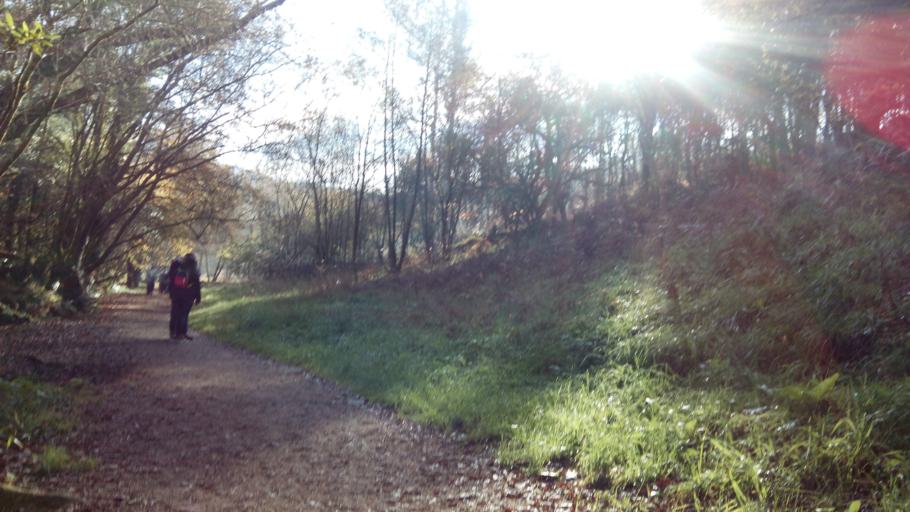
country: ES
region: Galicia
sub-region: Provincia de Pontevedra
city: Meis
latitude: 42.4853
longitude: -8.7449
